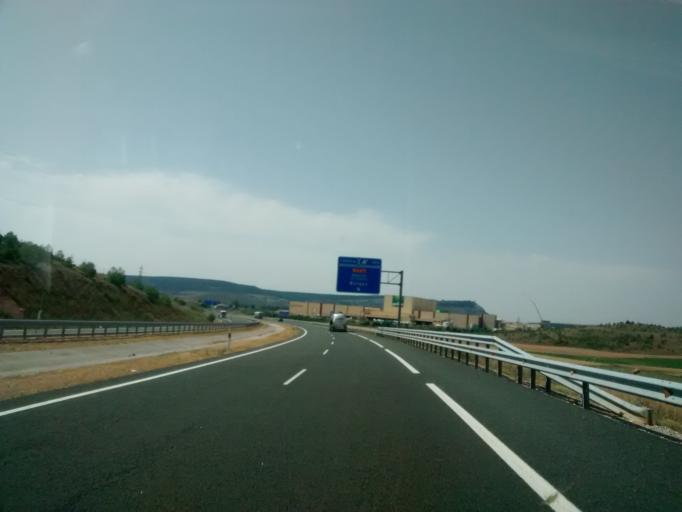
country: ES
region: Castille and Leon
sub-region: Provincia de Palencia
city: Aguilar de Campoo
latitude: 42.7974
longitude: -4.2370
